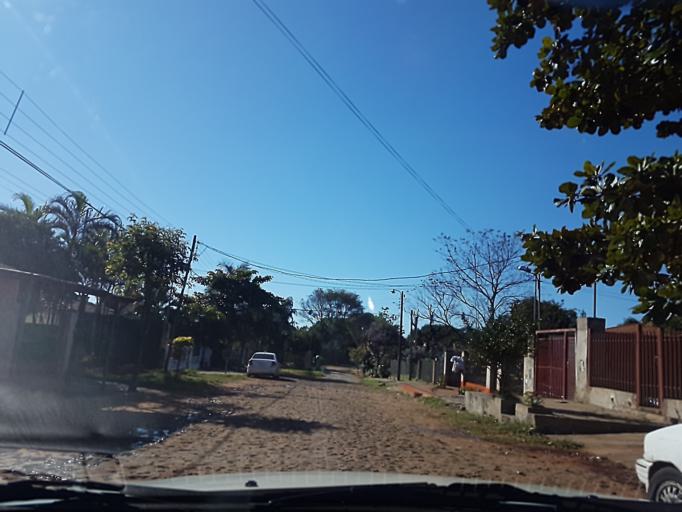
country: PY
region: Central
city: Nemby
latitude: -25.3969
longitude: -57.5435
